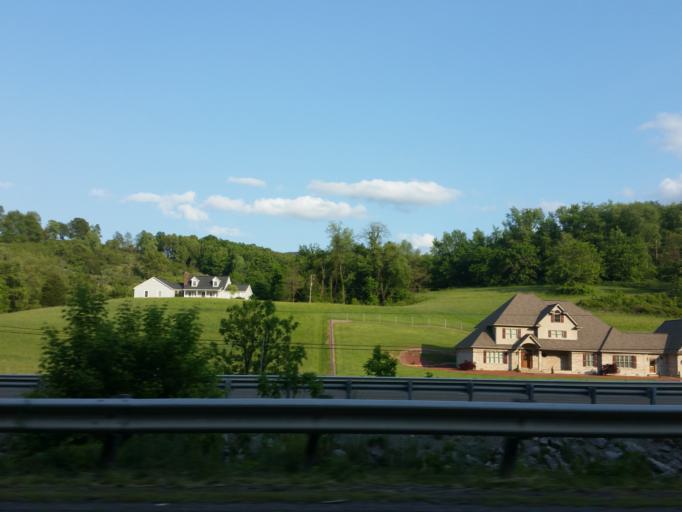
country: US
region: Virginia
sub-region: Tazewell County
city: Raven
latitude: 36.9881
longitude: -81.8476
